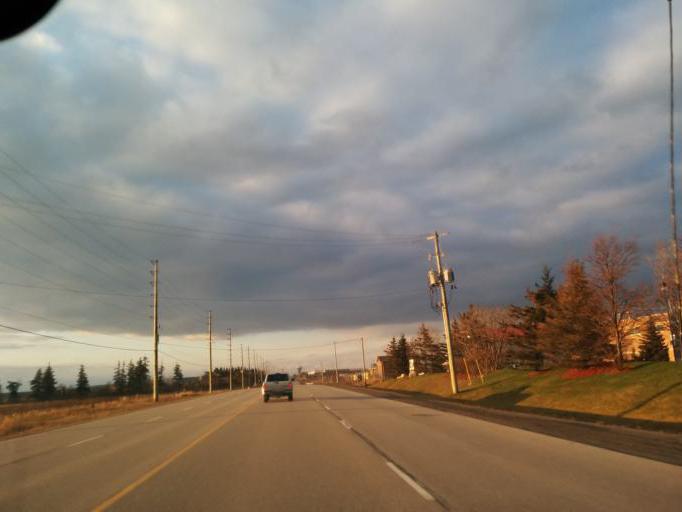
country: CA
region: Ontario
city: Brampton
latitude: 43.8513
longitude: -79.7228
